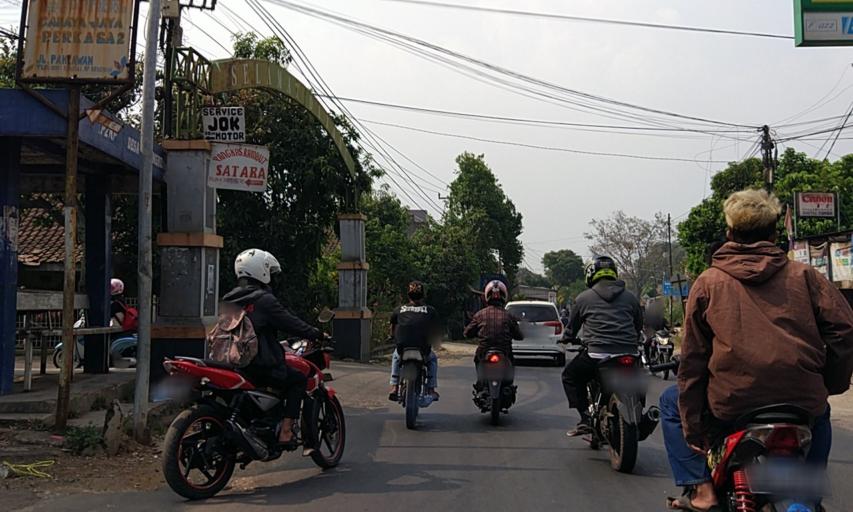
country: ID
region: West Java
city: Banjaran
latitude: -7.0553
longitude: 107.5704
